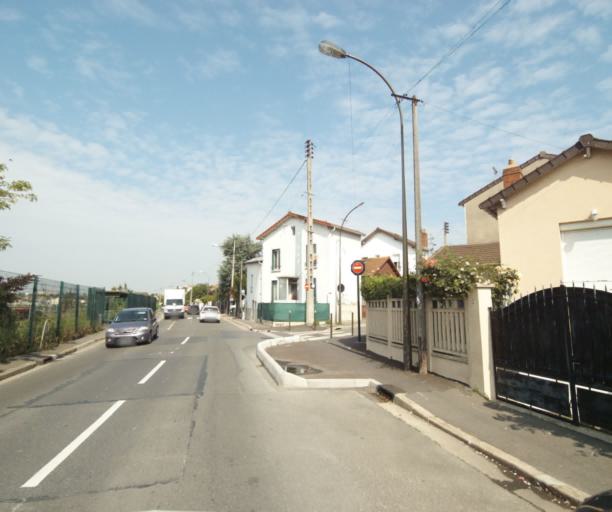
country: FR
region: Ile-de-France
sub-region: Departement du Val-d'Oise
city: Argenteuil
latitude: 48.9559
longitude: 2.2508
